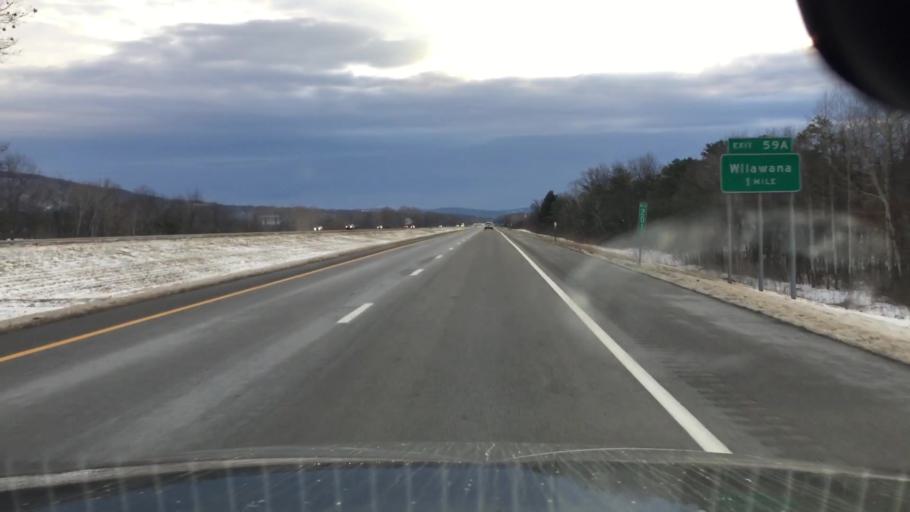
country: US
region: Pennsylvania
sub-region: Bradford County
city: South Waverly
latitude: 42.0009
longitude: -76.6138
